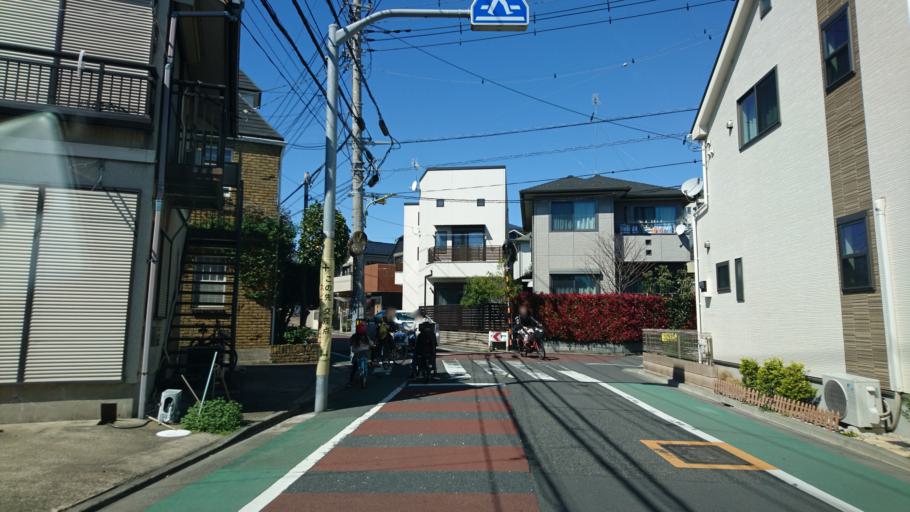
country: JP
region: Kanagawa
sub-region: Kawasaki-shi
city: Kawasaki
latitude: 35.5780
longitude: 139.7106
